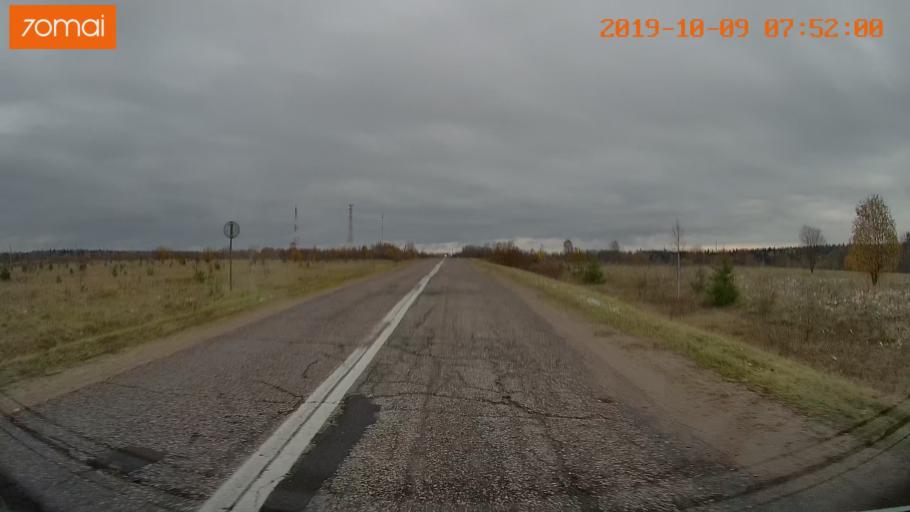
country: RU
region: Jaroslavl
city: Kukoboy
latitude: 58.6876
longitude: 39.8829
